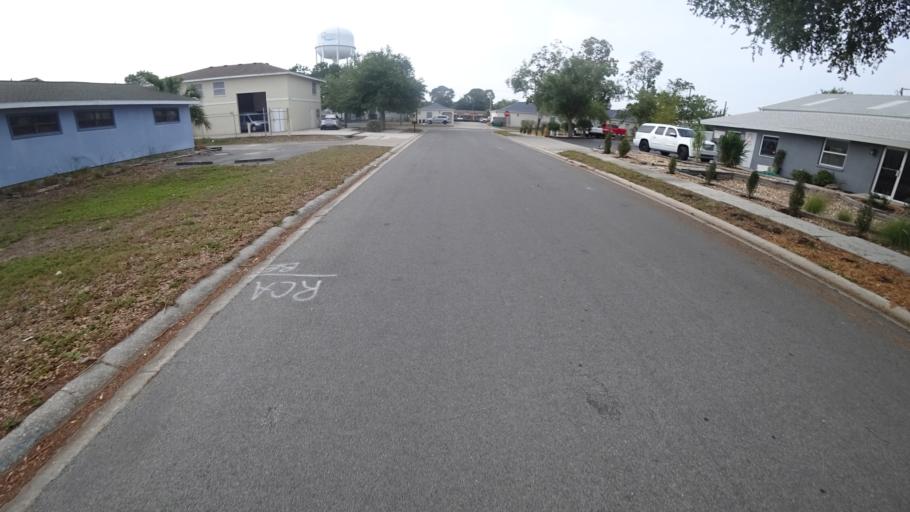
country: US
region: Florida
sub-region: Manatee County
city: West Bradenton
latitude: 27.4637
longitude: -82.6213
